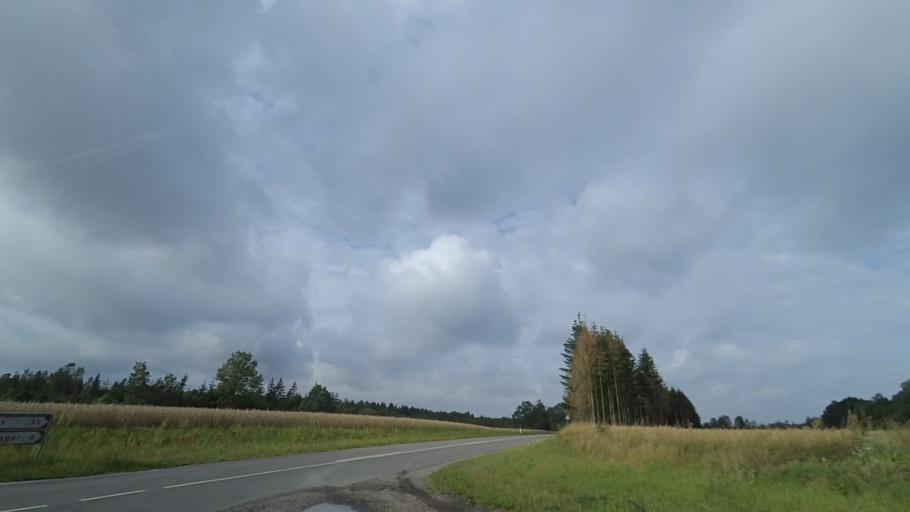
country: DK
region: Central Jutland
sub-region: Syddjurs Kommune
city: Ryomgard
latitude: 56.3563
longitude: 10.5202
